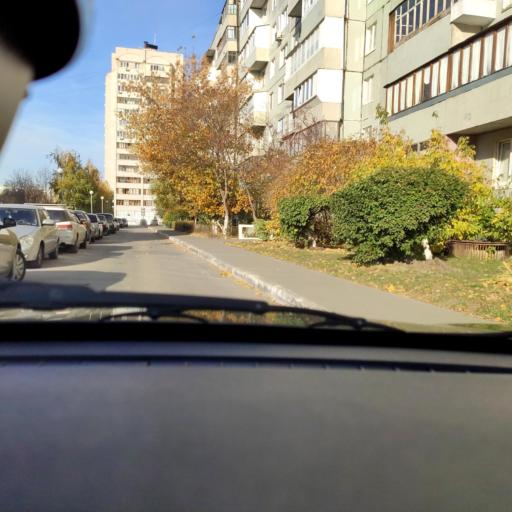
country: RU
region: Samara
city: Tol'yatti
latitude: 53.5422
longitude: 49.3516
